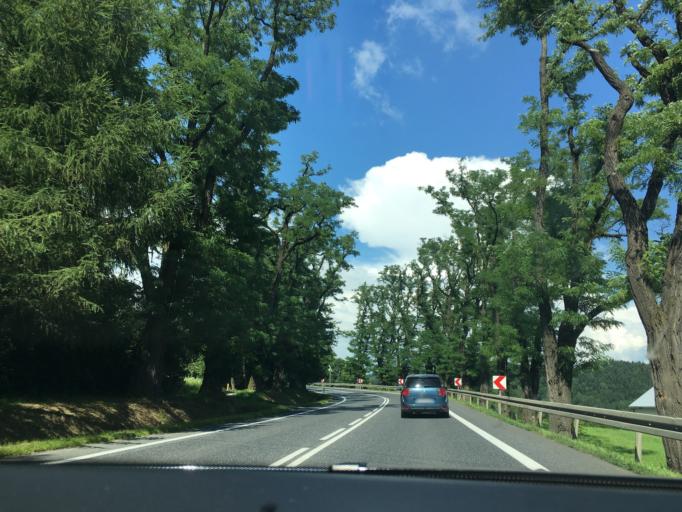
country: PL
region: Subcarpathian Voivodeship
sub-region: Powiat krosnienski
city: Dukla
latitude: 49.5620
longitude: 21.6896
